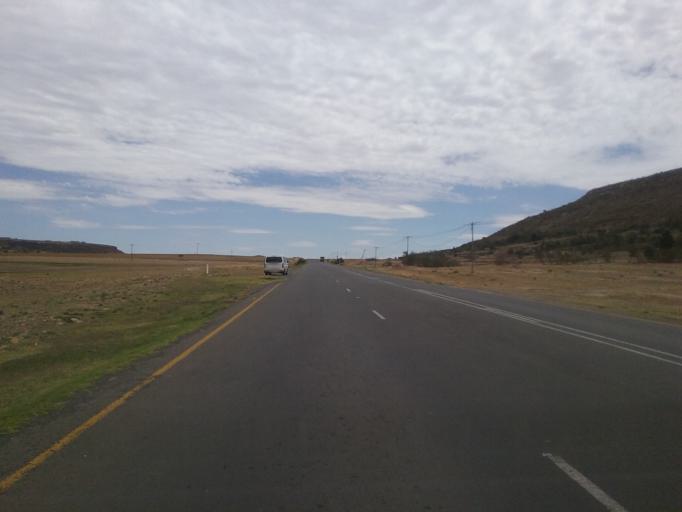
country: LS
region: Maseru
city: Nako
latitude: -29.6074
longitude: 27.5012
